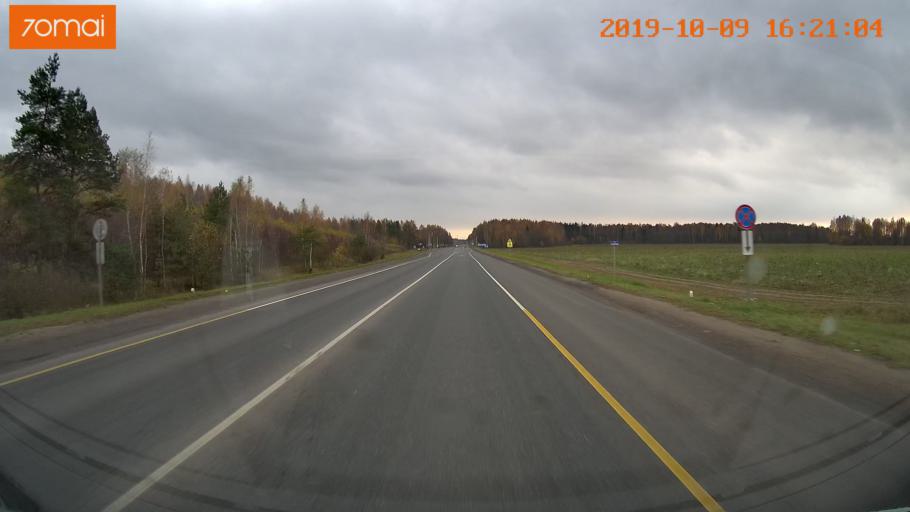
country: RU
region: Kostroma
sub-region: Kostromskoy Rayon
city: Kostroma
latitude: 57.6978
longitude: 40.8904
